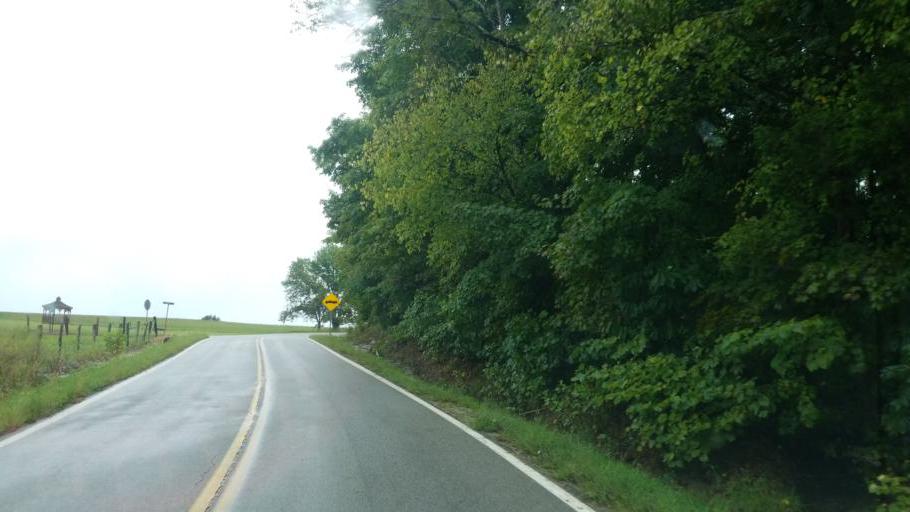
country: US
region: Ohio
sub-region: Adams County
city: West Union
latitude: 38.7371
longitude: -83.5180
